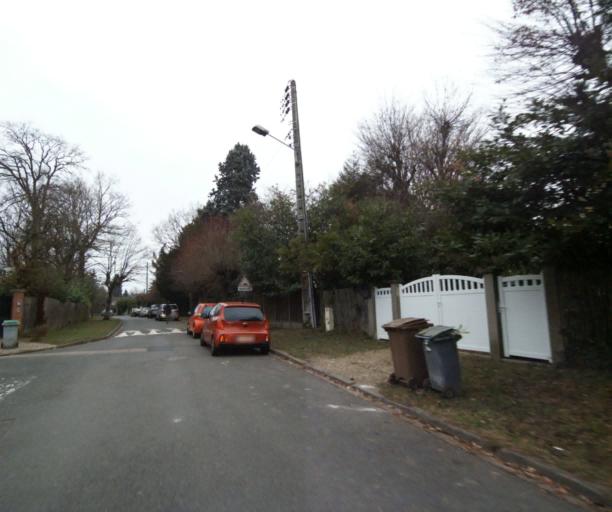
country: FR
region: Ile-de-France
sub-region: Departement des Hauts-de-Seine
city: Vaucresson
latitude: 48.8420
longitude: 2.1568
